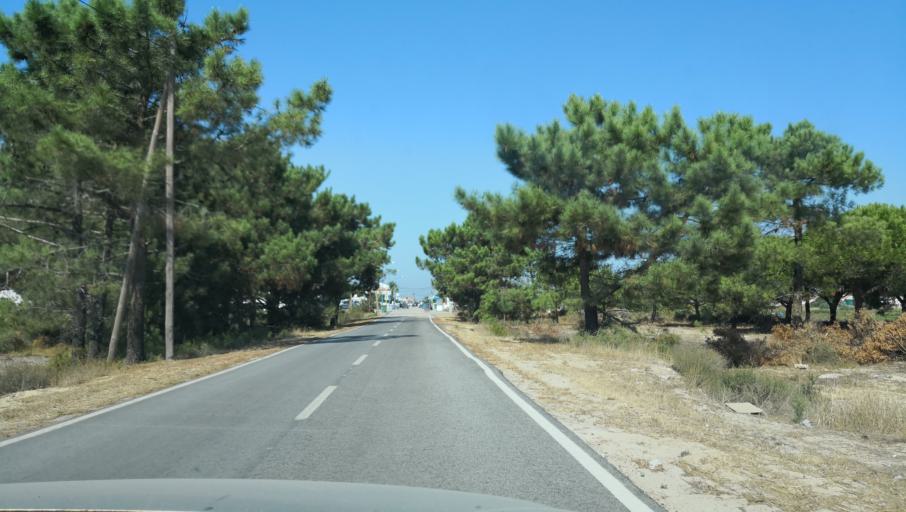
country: PT
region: Setubal
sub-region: Setubal
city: Setubal
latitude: 38.4061
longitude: -8.7468
